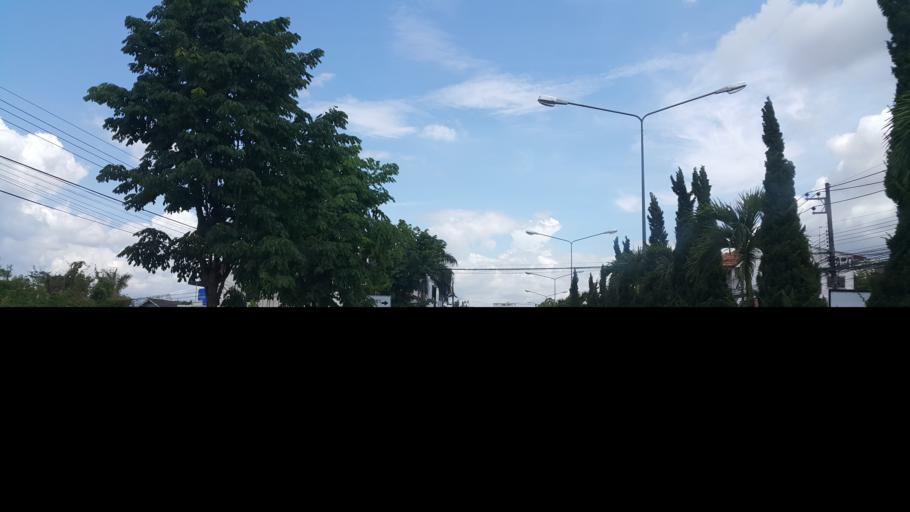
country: TH
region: Phayao
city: Phayao
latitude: 19.1824
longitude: 99.8825
